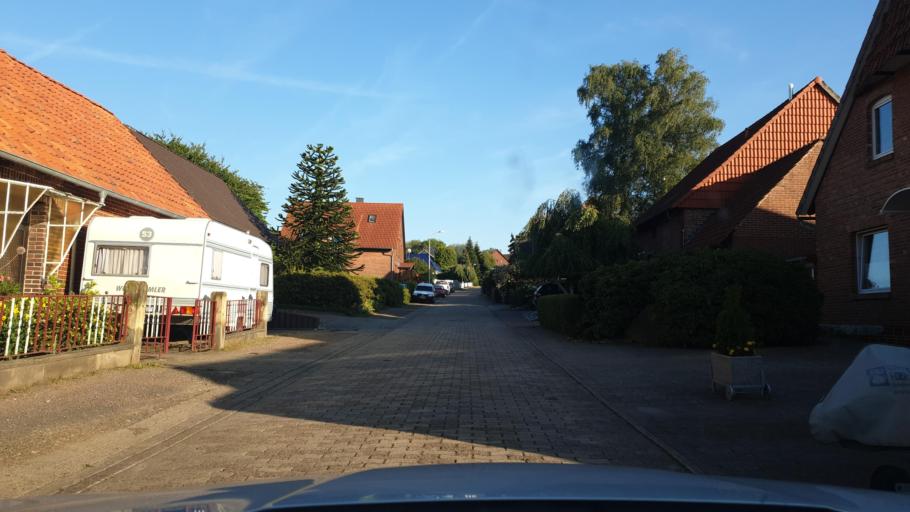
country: DE
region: Lower Saxony
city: Nienstadt
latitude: 52.2940
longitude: 9.1721
